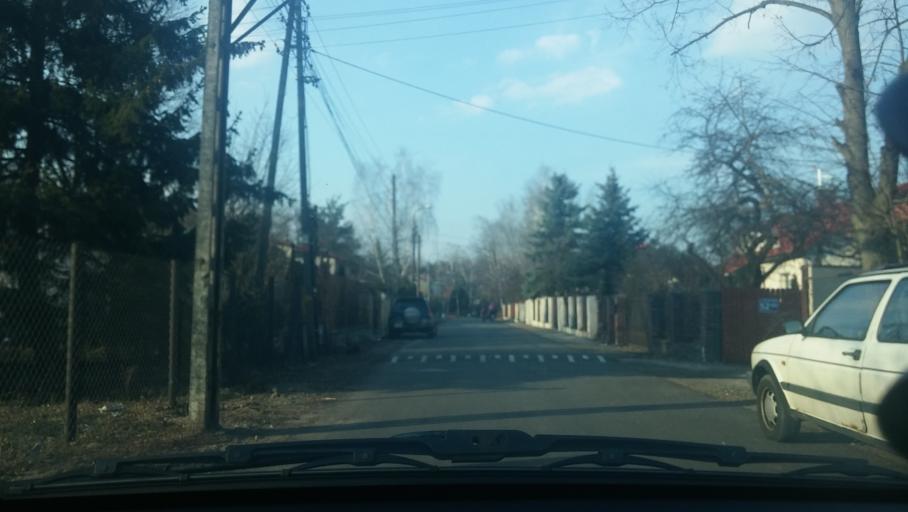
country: PL
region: Masovian Voivodeship
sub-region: Warszawa
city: Wawer
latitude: 52.2047
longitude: 21.1626
